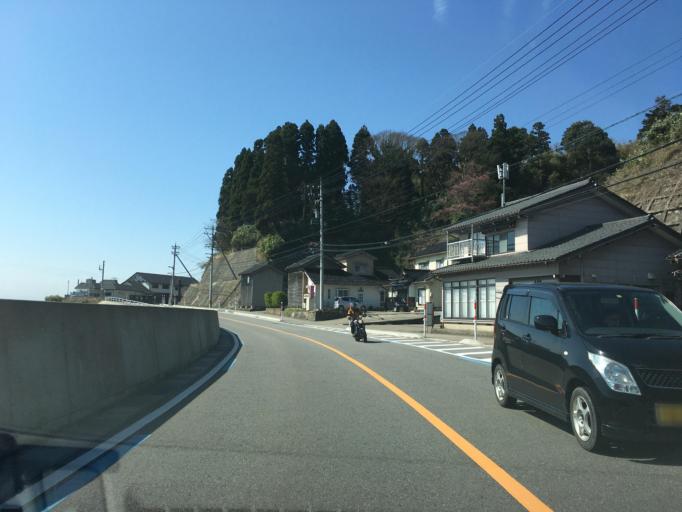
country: JP
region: Toyama
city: Himi
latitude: 36.9012
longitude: 137.0117
